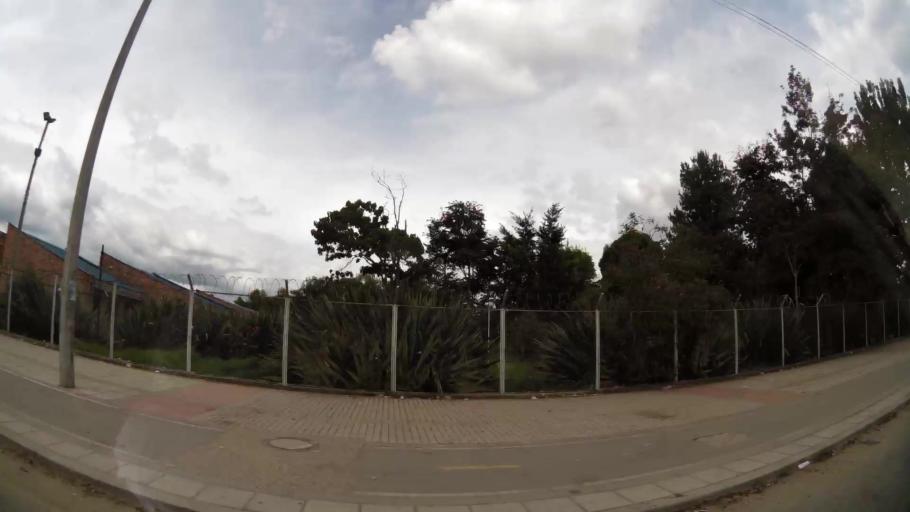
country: CO
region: Cundinamarca
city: Funza
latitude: 4.7208
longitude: -74.1435
